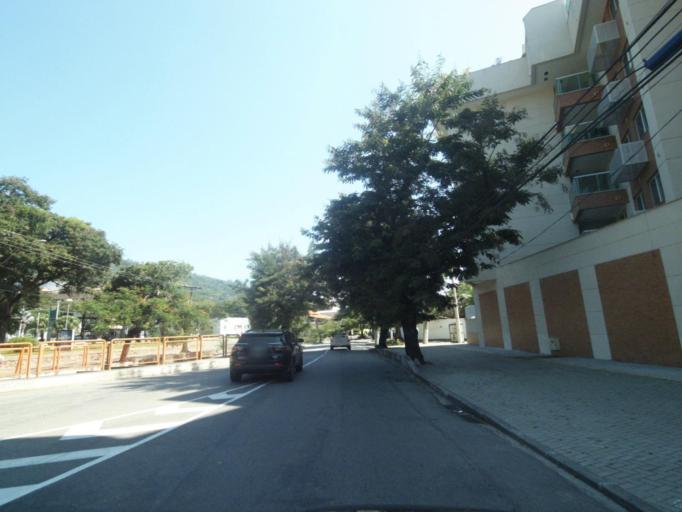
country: BR
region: Rio de Janeiro
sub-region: Niteroi
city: Niteroi
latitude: -22.9133
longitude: -43.0823
